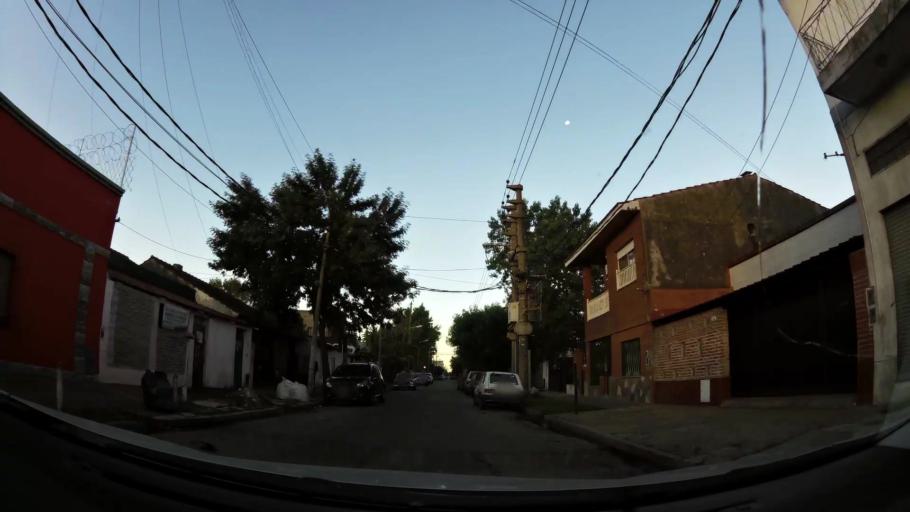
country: AR
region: Buenos Aires
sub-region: Partido de Tigre
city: Tigre
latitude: -34.4441
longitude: -58.5731
